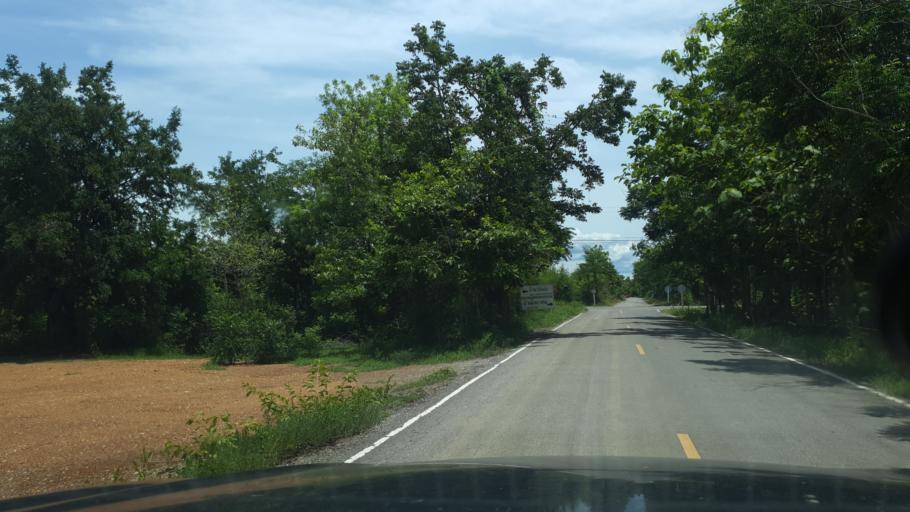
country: TH
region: Sukhothai
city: Ban Na
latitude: 17.1076
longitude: 99.6783
